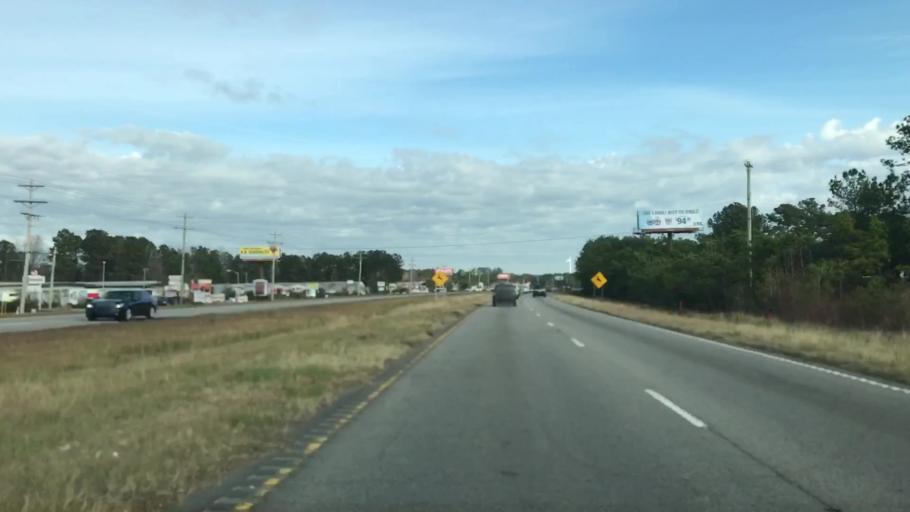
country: US
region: South Carolina
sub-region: Horry County
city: Garden City
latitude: 33.5897
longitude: -79.0262
